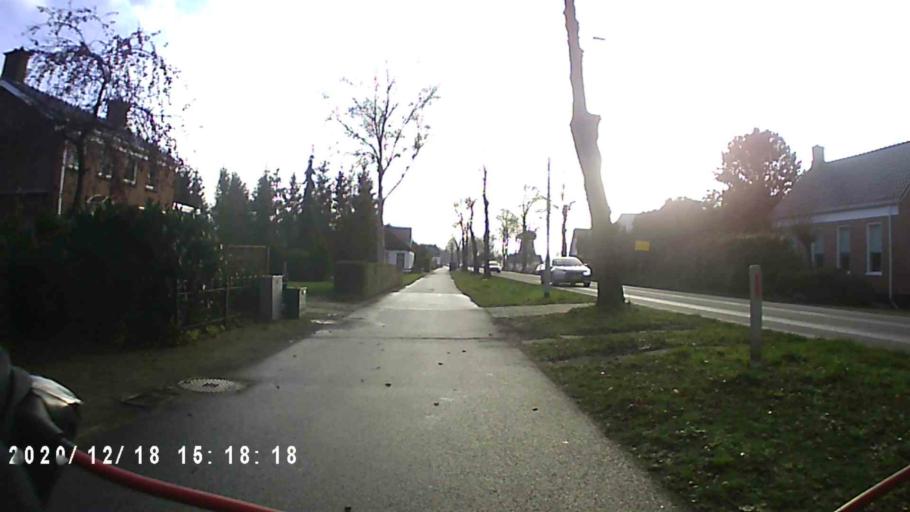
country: NL
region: Groningen
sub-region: Gemeente Hoogezand-Sappemeer
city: Hoogezand
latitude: 53.1608
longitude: 6.7229
